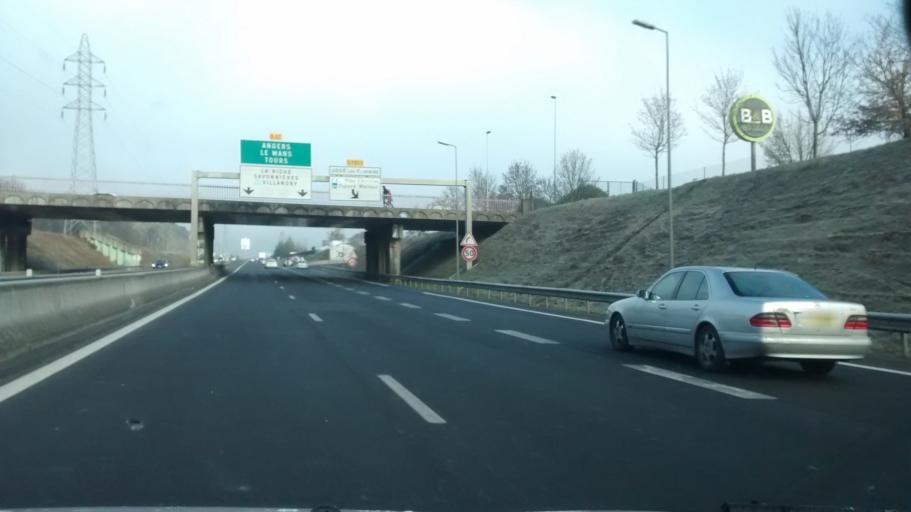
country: FR
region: Centre
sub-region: Departement d'Indre-et-Loire
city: Joue-les-Tours
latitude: 47.3456
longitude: 0.6462
